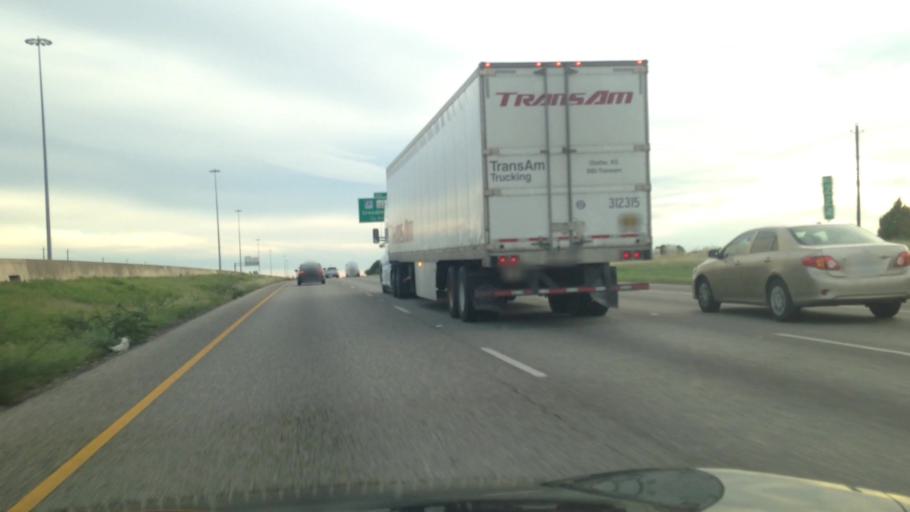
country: US
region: Texas
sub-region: Travis County
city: Onion Creek
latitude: 30.1264
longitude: -97.8015
